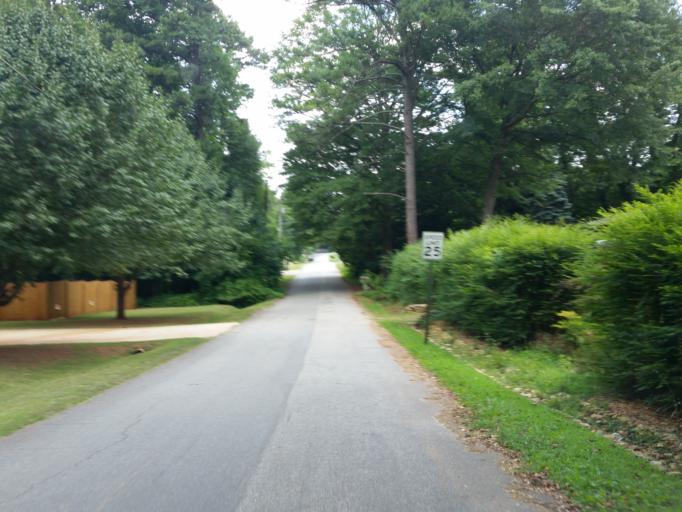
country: US
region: Georgia
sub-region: Cobb County
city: Marietta
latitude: 33.9973
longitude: -84.5207
